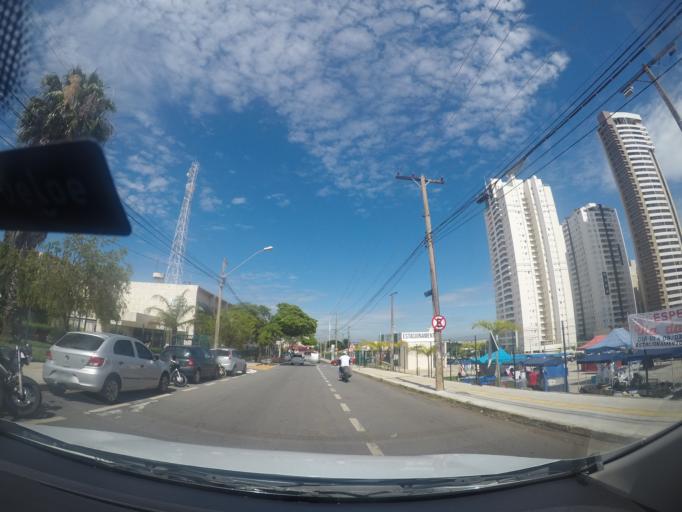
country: BR
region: Goias
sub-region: Goiania
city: Goiania
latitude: -16.7220
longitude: -49.2648
